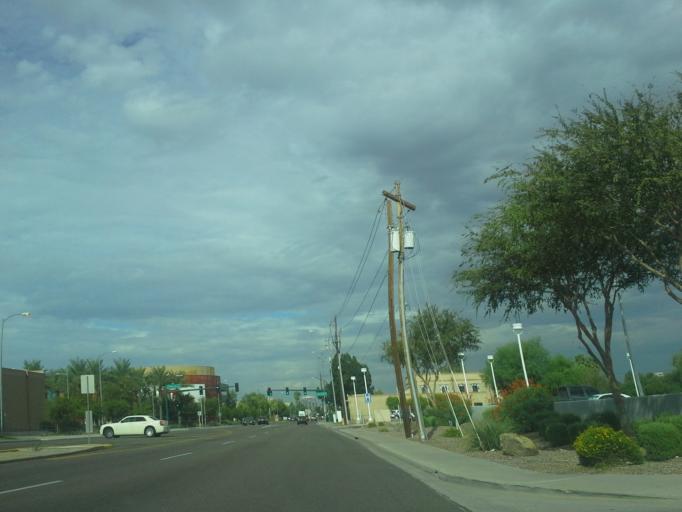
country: US
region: Arizona
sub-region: Maricopa County
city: Phoenix
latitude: 33.4804
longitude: -112.0401
